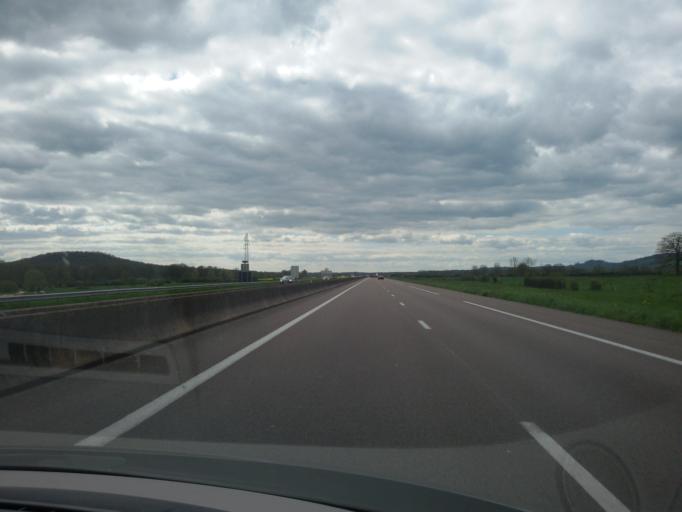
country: FR
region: Bourgogne
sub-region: Departement de la Cote-d'Or
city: Pouilly-en-Auxois
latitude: 47.2998
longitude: 4.5039
